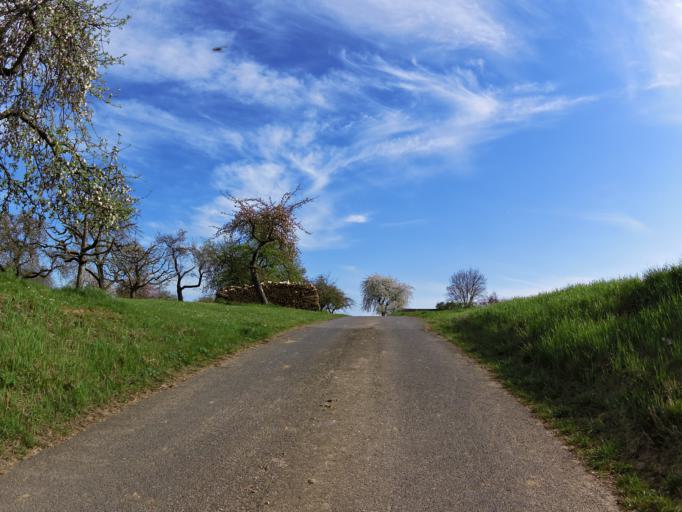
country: DE
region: Bavaria
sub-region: Regierungsbezirk Unterfranken
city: Unterpleichfeld
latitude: 49.8727
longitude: 10.0238
